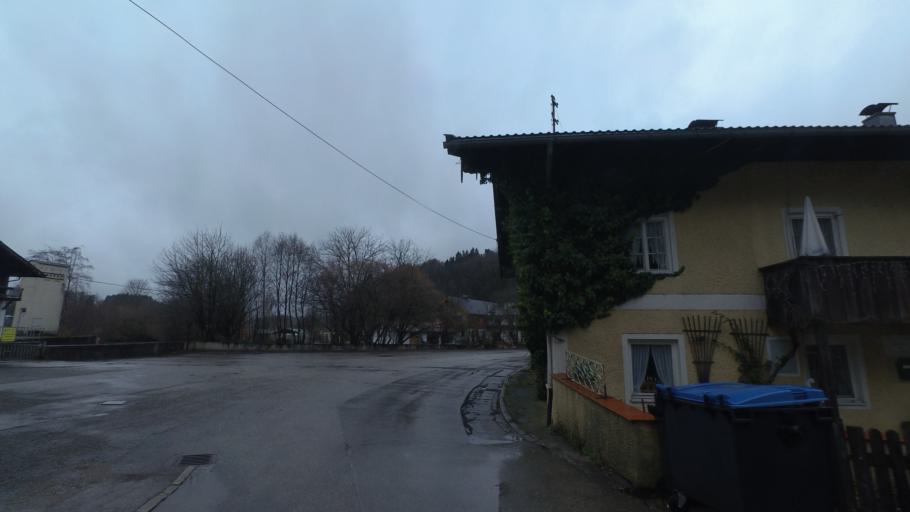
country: DE
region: Bavaria
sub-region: Upper Bavaria
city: Nussdorf
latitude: 47.9168
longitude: 12.6271
